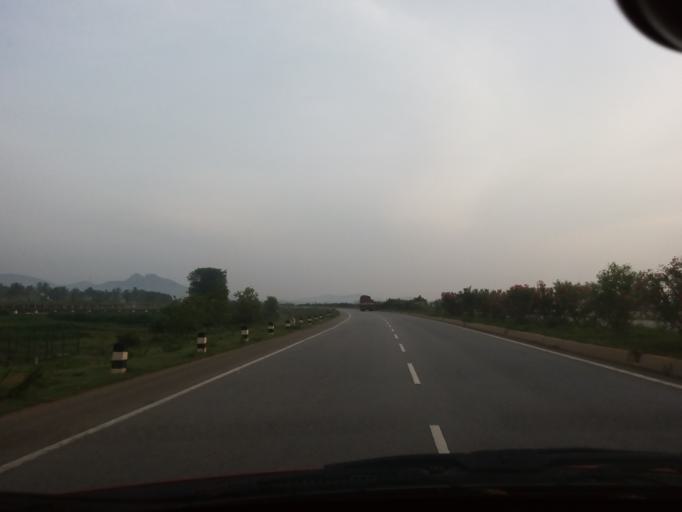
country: IN
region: Karnataka
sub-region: Chikkaballapur
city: Chik Ballapur
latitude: 13.4225
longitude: 77.7444
